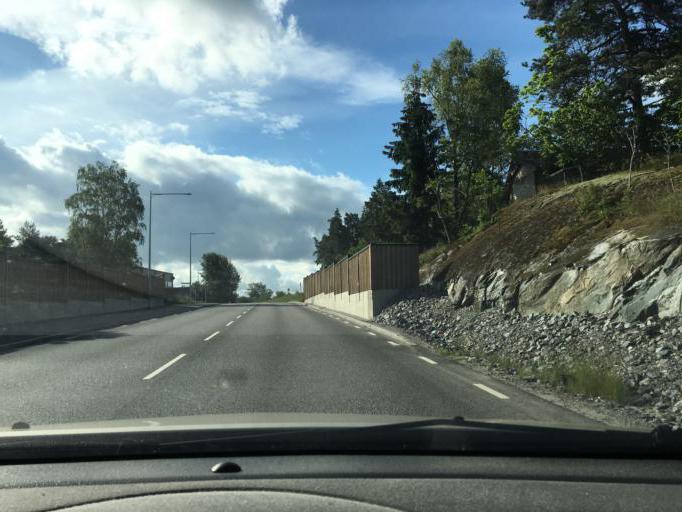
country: SE
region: Stockholm
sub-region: Sodertalje Kommun
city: Soedertaelje
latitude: 59.2111
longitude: 17.6561
